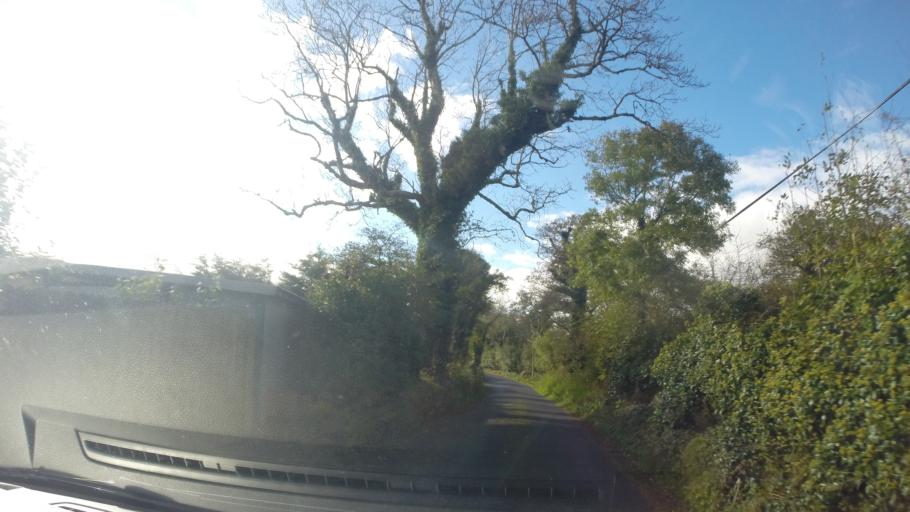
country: IE
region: Ulster
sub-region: County Donegal
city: Killybegs
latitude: 54.6289
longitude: -8.3730
